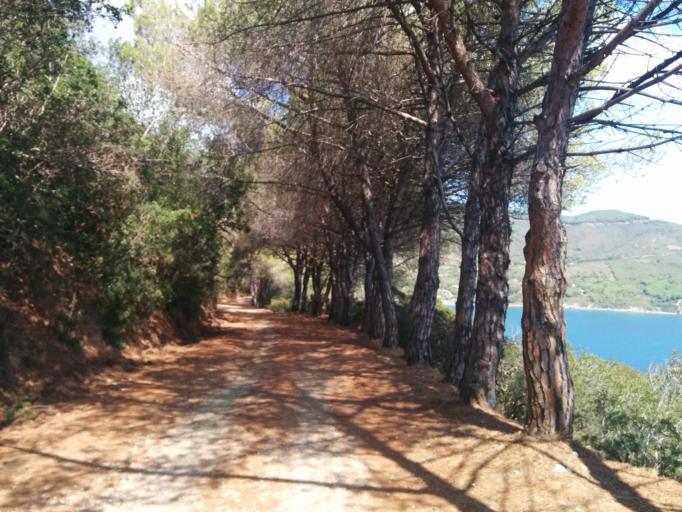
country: IT
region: Tuscany
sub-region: Provincia di Livorno
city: Capoliveri
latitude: 42.7512
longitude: 10.3193
